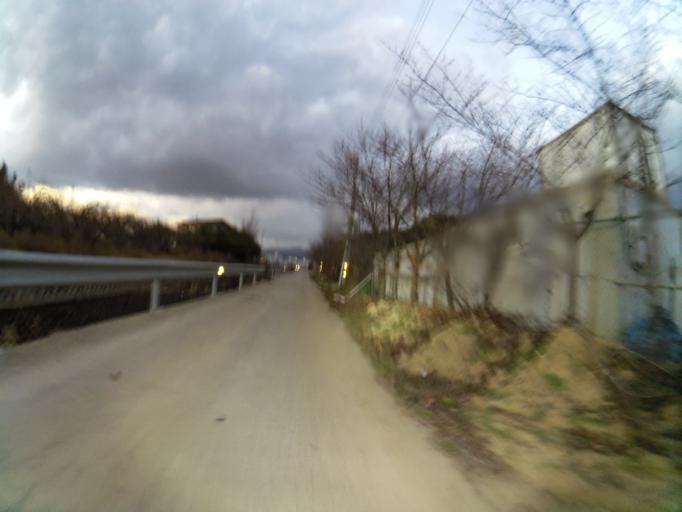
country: KR
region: Gyeongsangbuk-do
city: Gyeongsan-si
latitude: 35.8441
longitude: 128.7450
